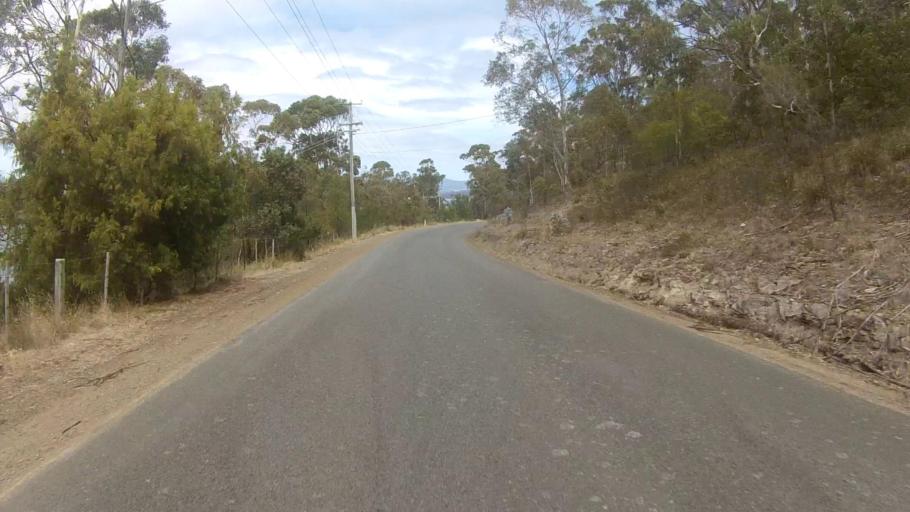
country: AU
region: Tasmania
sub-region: Kingborough
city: Blackmans Bay
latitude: -43.0516
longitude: 147.3400
